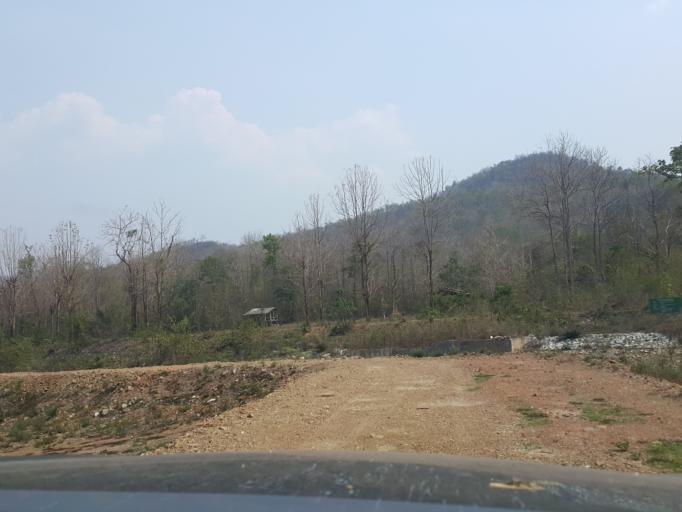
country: TH
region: Lampang
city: Mae Phrik
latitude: 17.5275
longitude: 98.9934
